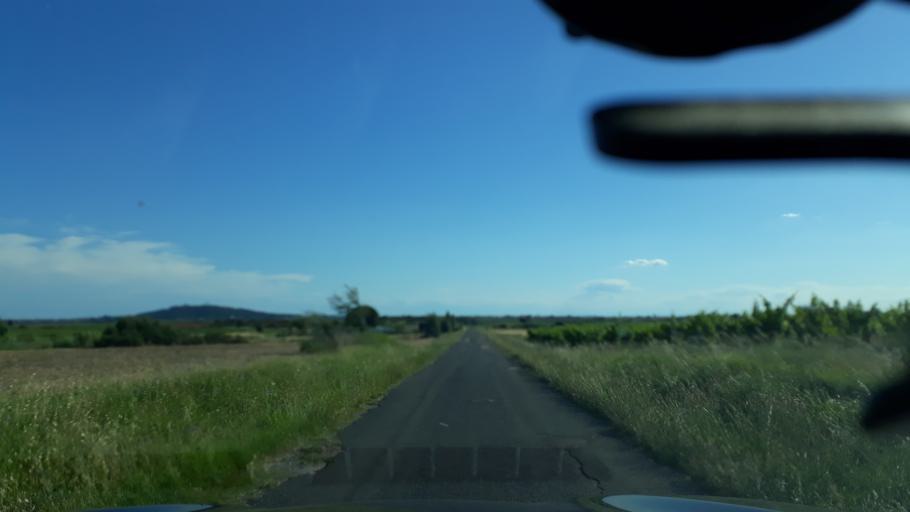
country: FR
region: Languedoc-Roussillon
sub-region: Departement de l'Herault
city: Marseillan
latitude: 43.3458
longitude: 3.5133
